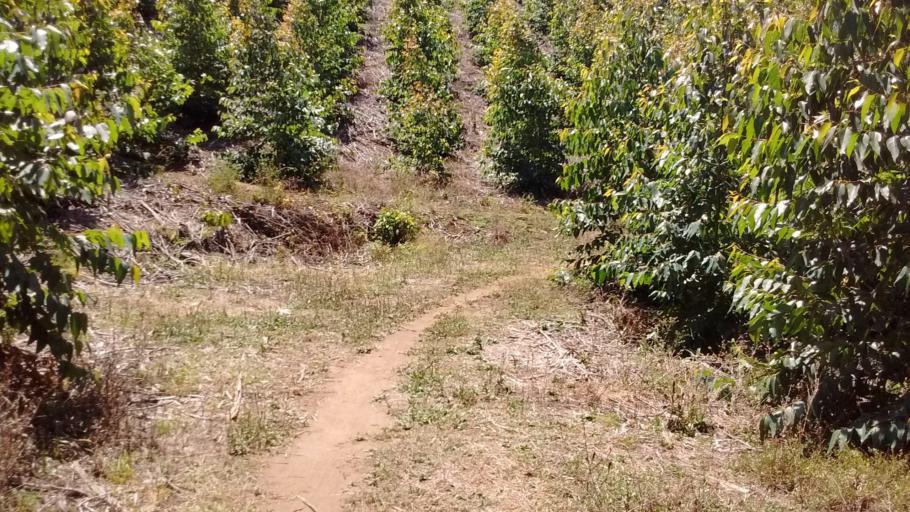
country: CO
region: Cauca
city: Popayan
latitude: 2.4588
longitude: -76.5660
